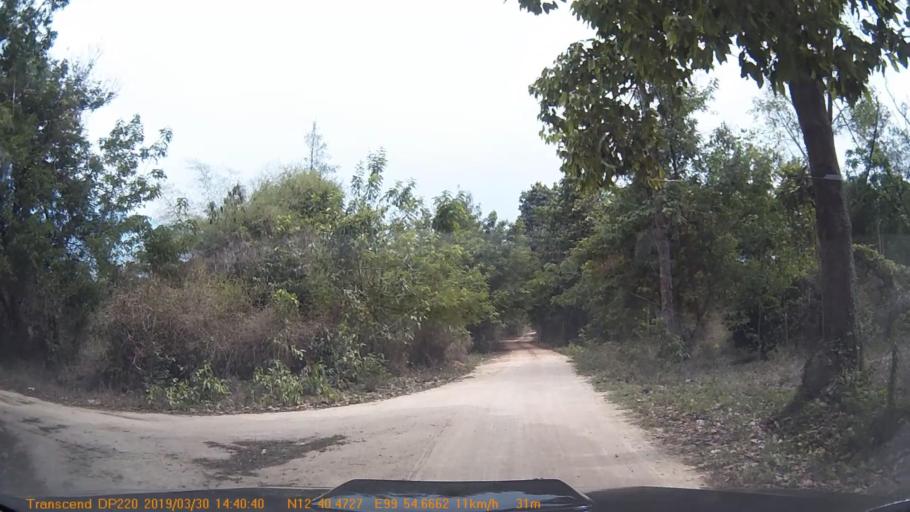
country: TH
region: Prachuap Khiri Khan
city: Hua Hin
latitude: 12.6745
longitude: 99.9112
